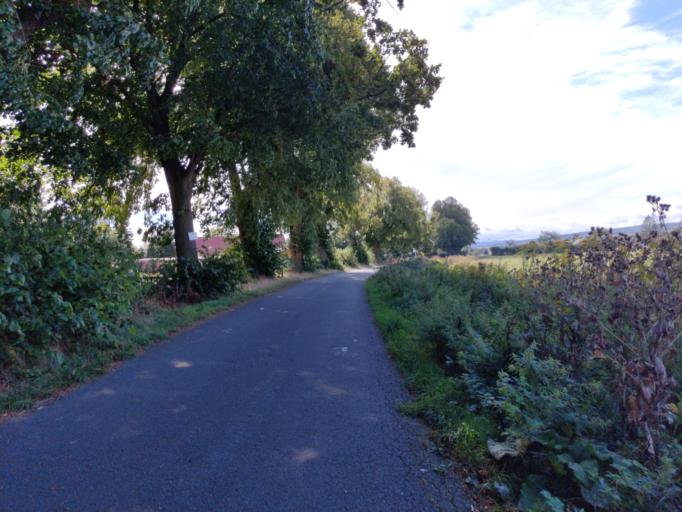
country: DE
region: Lower Saxony
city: Heere
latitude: 52.0703
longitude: 10.2550
